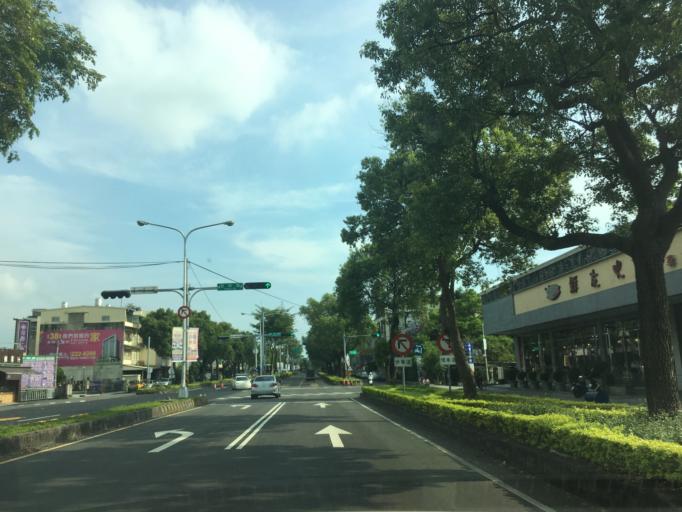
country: TW
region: Taiwan
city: Zhongxing New Village
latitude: 23.9813
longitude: 120.6811
